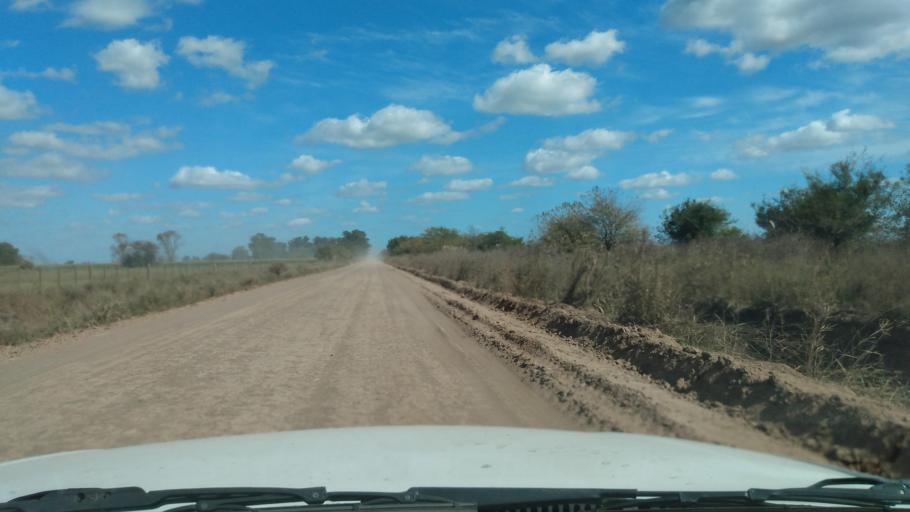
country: AR
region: Buenos Aires
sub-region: Partido de Navarro
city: Navarro
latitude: -35.0207
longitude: -59.4304
